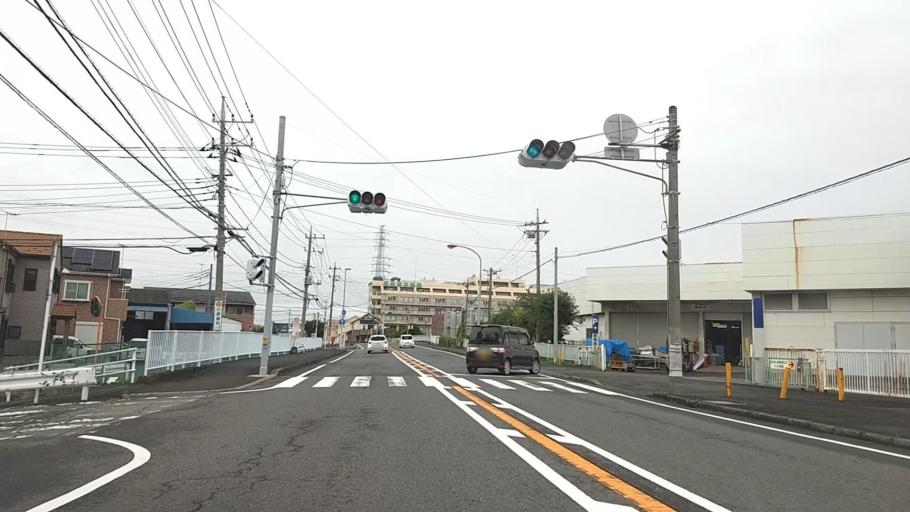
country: JP
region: Kanagawa
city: Atsugi
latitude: 35.4310
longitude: 139.3526
